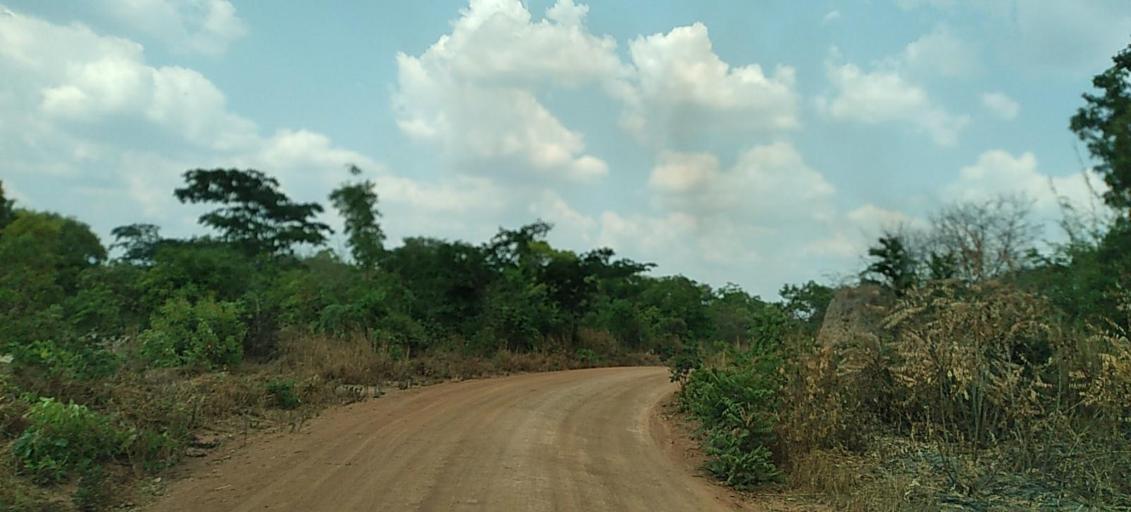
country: ZM
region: Copperbelt
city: Luanshya
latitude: -13.1403
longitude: 28.3315
